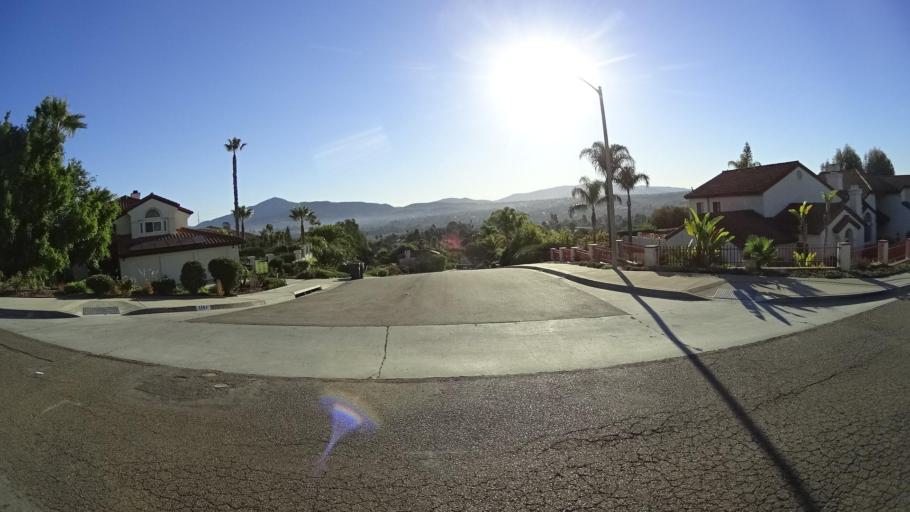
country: US
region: California
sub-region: San Diego County
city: Bonita
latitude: 32.6754
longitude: -117.0340
